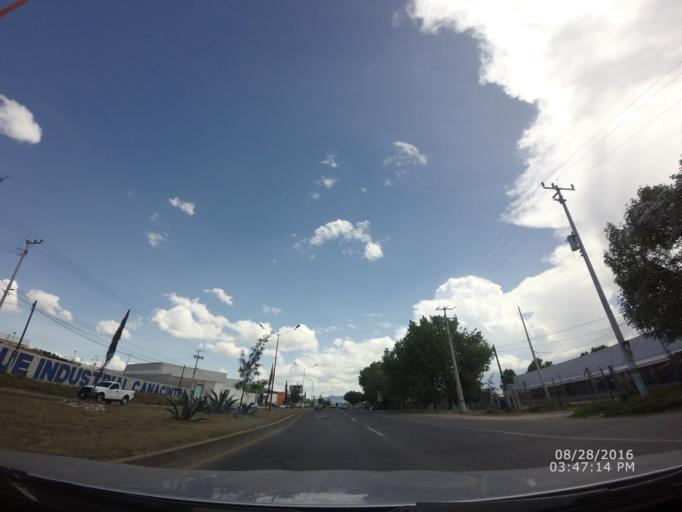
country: MX
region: Hidalgo
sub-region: Mineral de la Reforma
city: Nuevo Centro de Poblacion Agricola el Chacon
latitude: 20.0672
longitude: -98.7444
